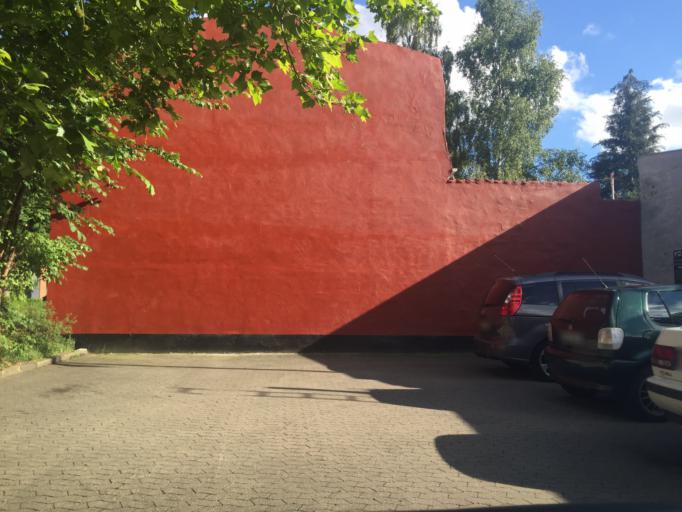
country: DK
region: Capital Region
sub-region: Kobenhavn
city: Vanlose
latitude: 55.7050
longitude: 12.5060
